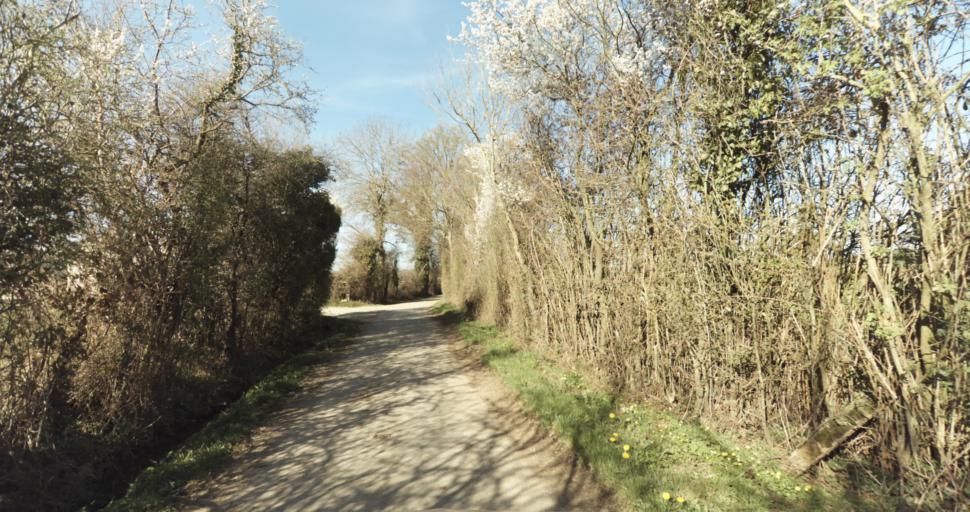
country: FR
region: Lower Normandy
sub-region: Departement du Calvados
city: Saint-Pierre-sur-Dives
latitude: 49.0509
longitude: 0.0556
